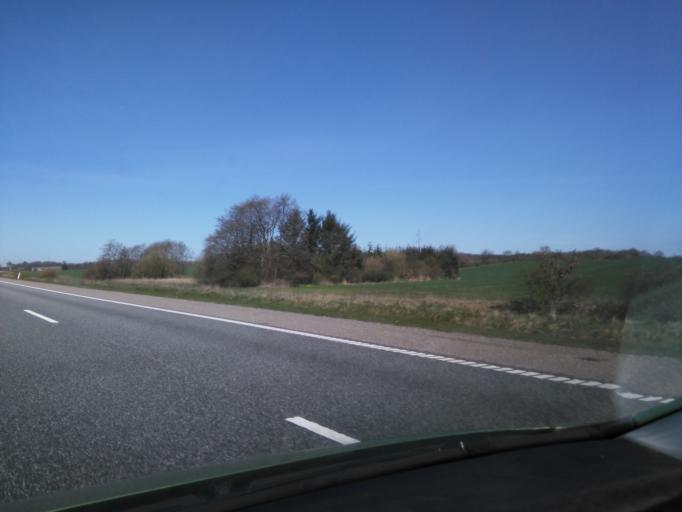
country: DK
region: Central Jutland
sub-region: Hedensted Kommune
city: Torring
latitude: 55.8330
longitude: 9.4664
